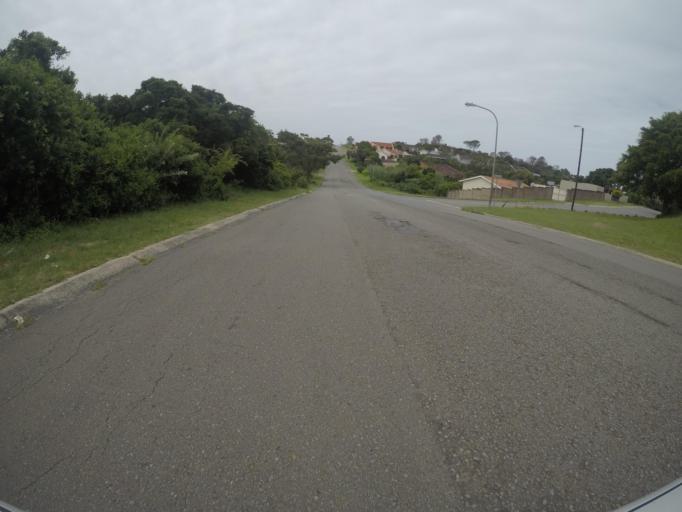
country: ZA
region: Eastern Cape
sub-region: Buffalo City Metropolitan Municipality
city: East London
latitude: -32.9739
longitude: 27.9458
